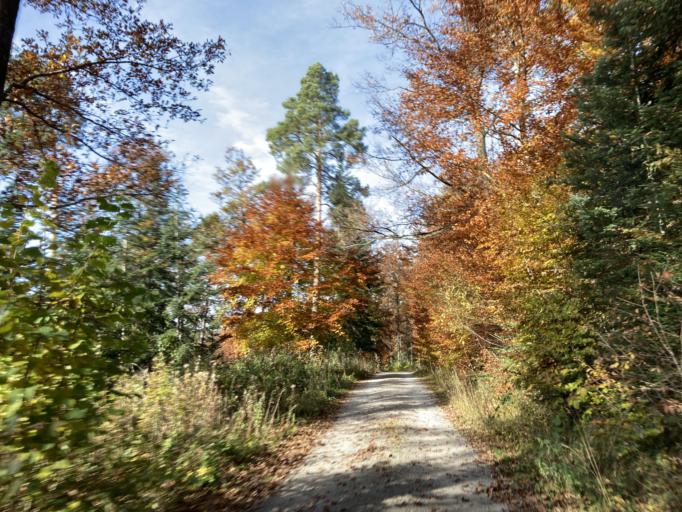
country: DE
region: Baden-Wuerttemberg
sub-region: Tuebingen Region
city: Rottenburg
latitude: 48.4444
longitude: 8.9406
